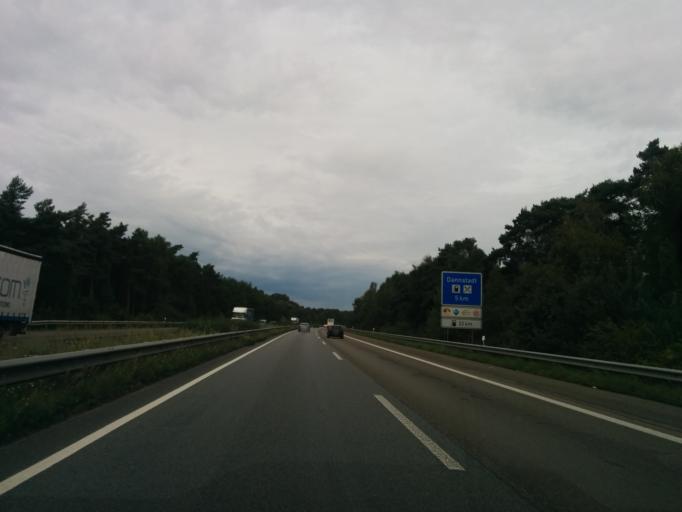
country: DE
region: Rheinland-Pfalz
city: Schifferstadt
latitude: 49.3645
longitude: 8.3561
